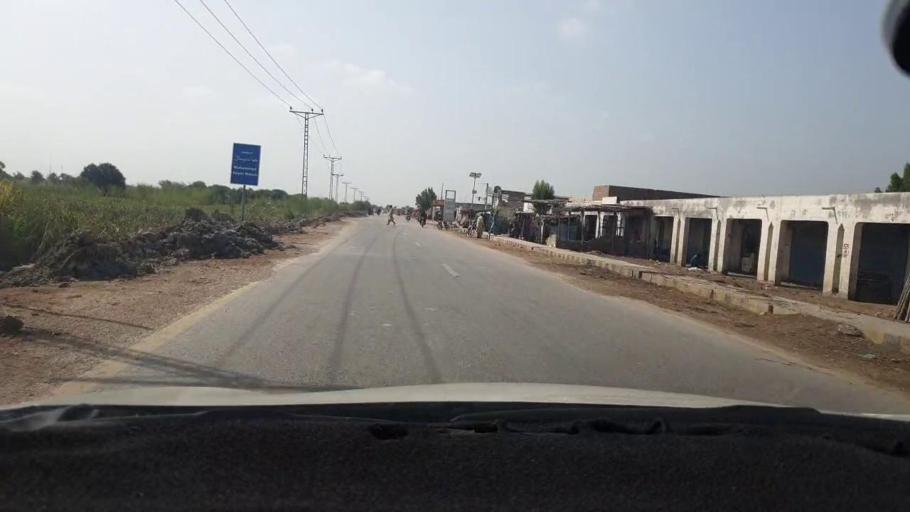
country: PK
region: Sindh
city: Mirpur Khas
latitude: 25.7723
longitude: 69.0713
